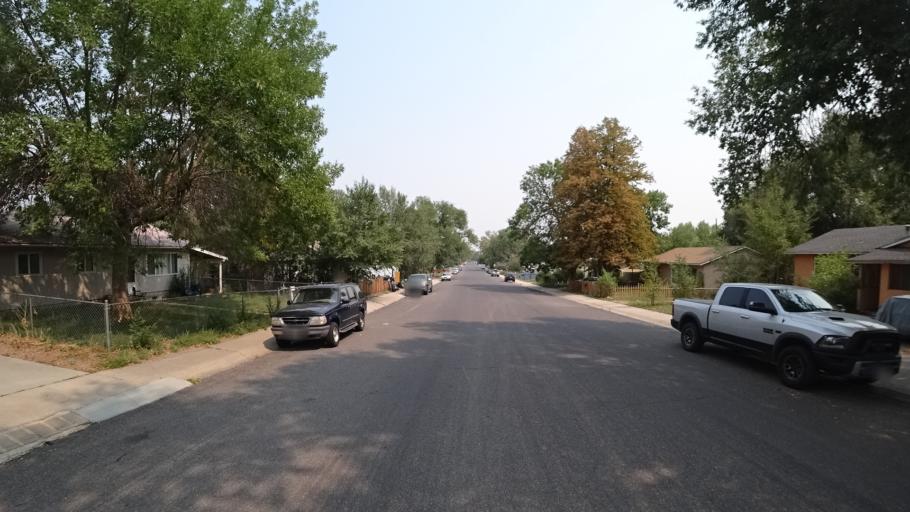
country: US
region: Colorado
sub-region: El Paso County
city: Colorado Springs
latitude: 38.8002
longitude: -104.8142
